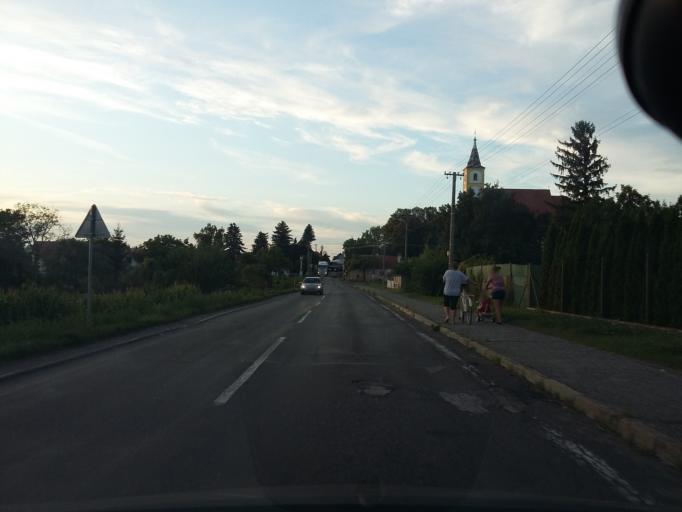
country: SK
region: Bratislavsky
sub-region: Okres Malacky
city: Malacky
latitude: 48.4046
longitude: 17.1552
